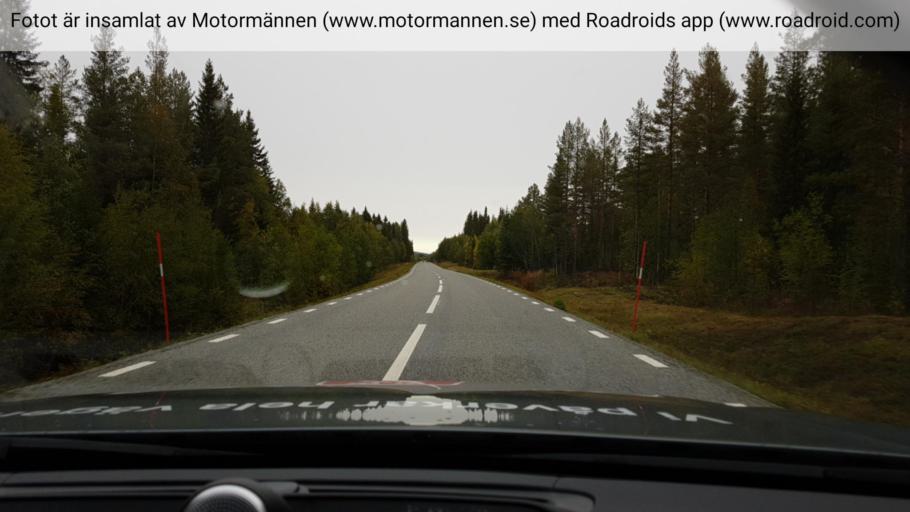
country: SE
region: Jaemtland
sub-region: Stroemsunds Kommun
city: Stroemsund
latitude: 63.9930
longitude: 15.5103
